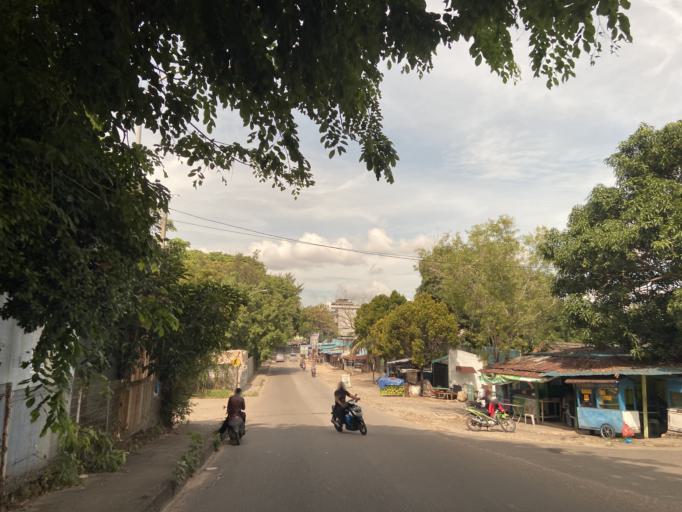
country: SG
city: Singapore
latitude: 1.1497
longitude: 104.0185
